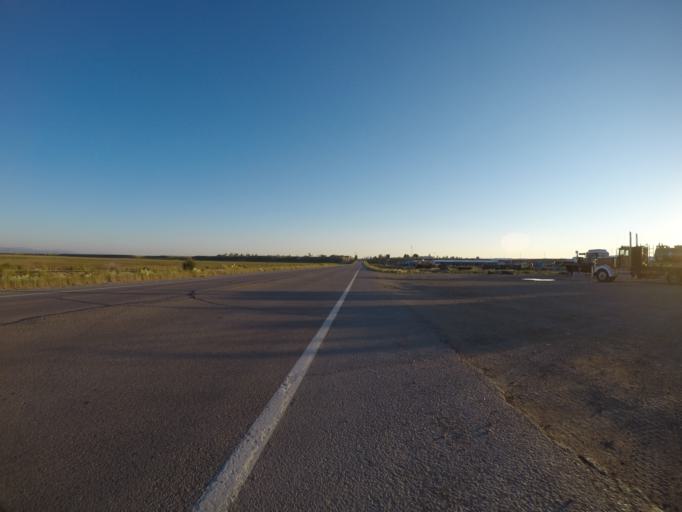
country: US
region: Wyoming
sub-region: Sublette County
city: Marbleton
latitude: 42.5445
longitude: -110.1096
